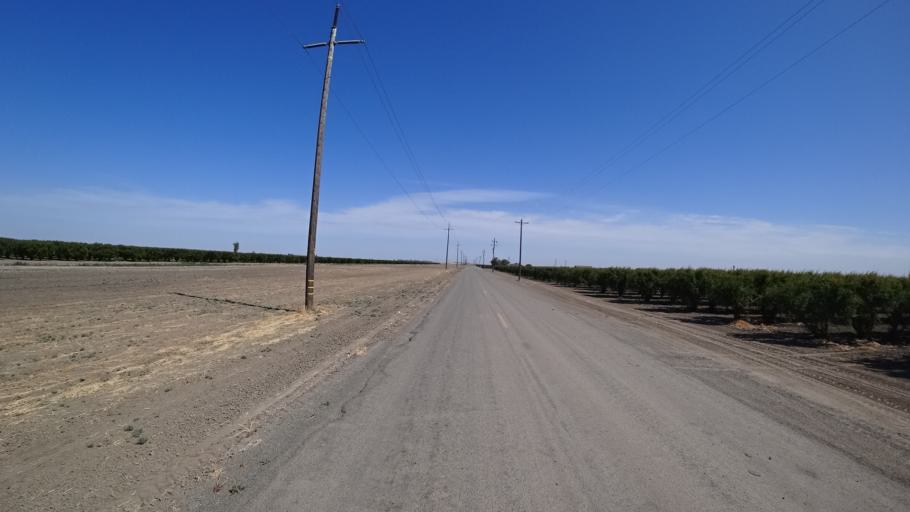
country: US
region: California
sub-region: Kings County
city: Stratford
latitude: 36.2482
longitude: -119.8345
